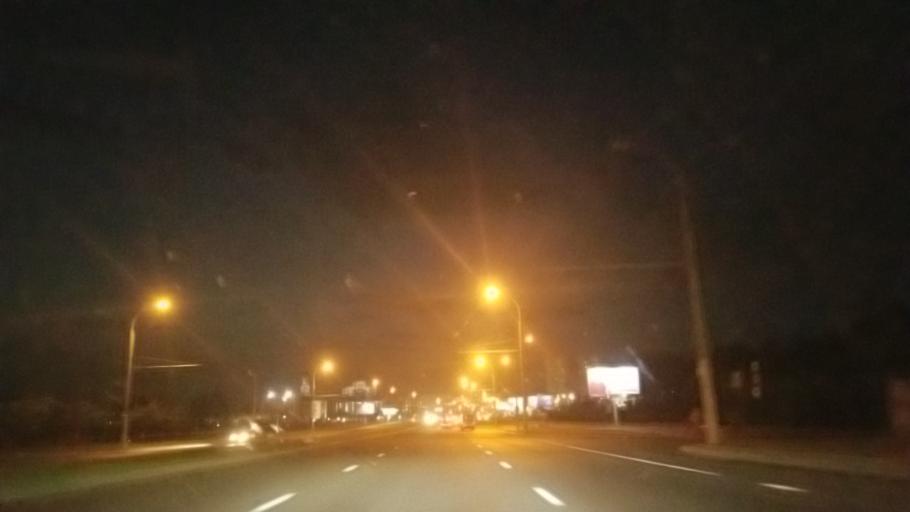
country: BY
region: Brest
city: Brest
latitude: 52.0930
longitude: 23.7682
